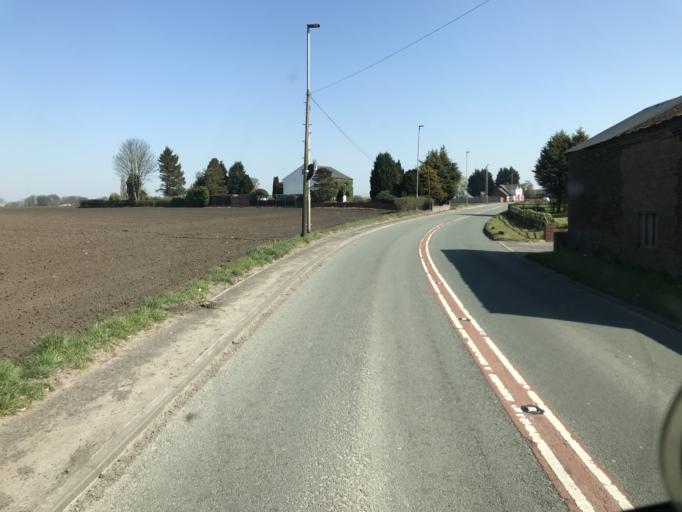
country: GB
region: England
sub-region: Warrington
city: Lymm
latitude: 53.4001
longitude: -2.5012
